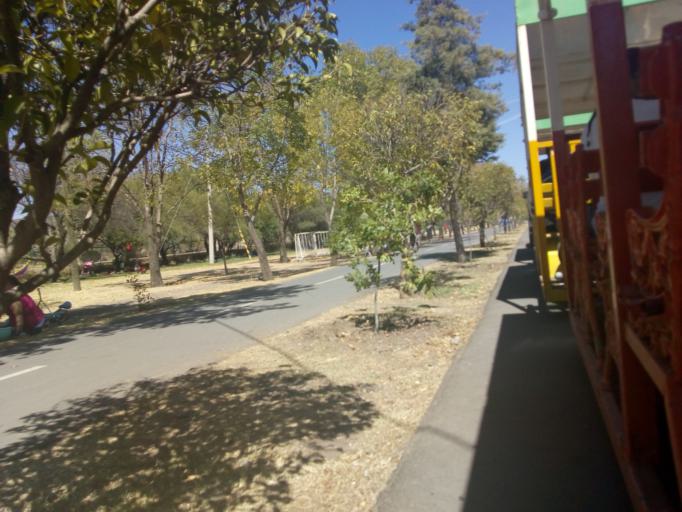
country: MX
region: Guanajuato
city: Leon
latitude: 21.1886
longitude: -101.6831
